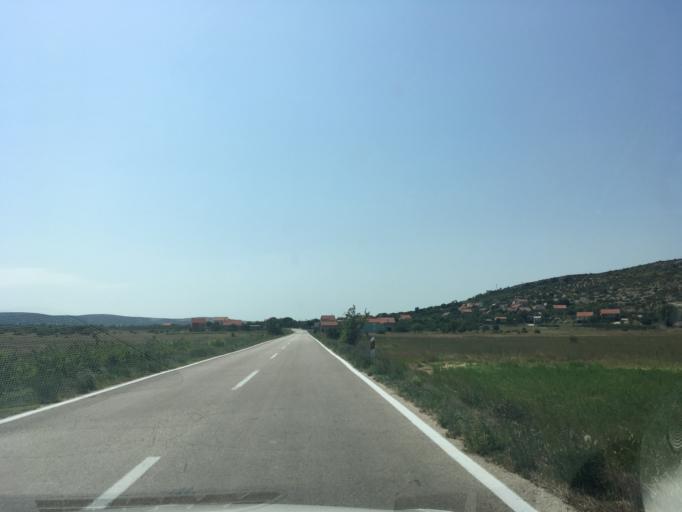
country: HR
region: Zadarska
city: Benkovac
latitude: 43.9633
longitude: 15.7575
